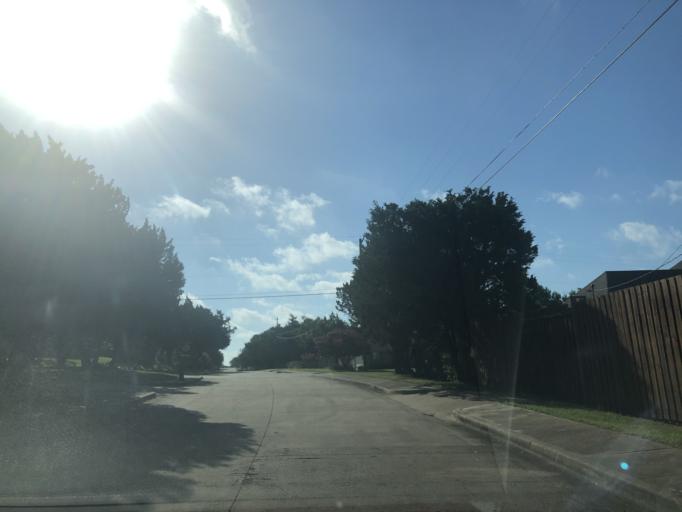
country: US
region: Texas
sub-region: Dallas County
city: Duncanville
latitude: 32.6574
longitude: -96.9330
